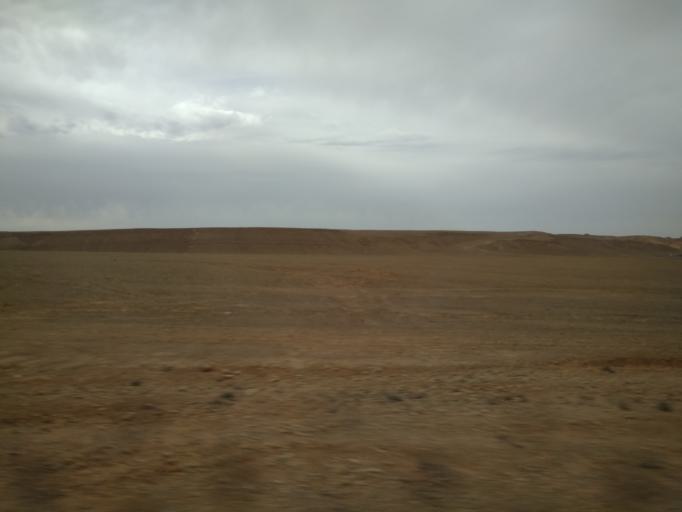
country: IL
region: Southern District
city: Eilat
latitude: 29.8532
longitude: 34.8421
